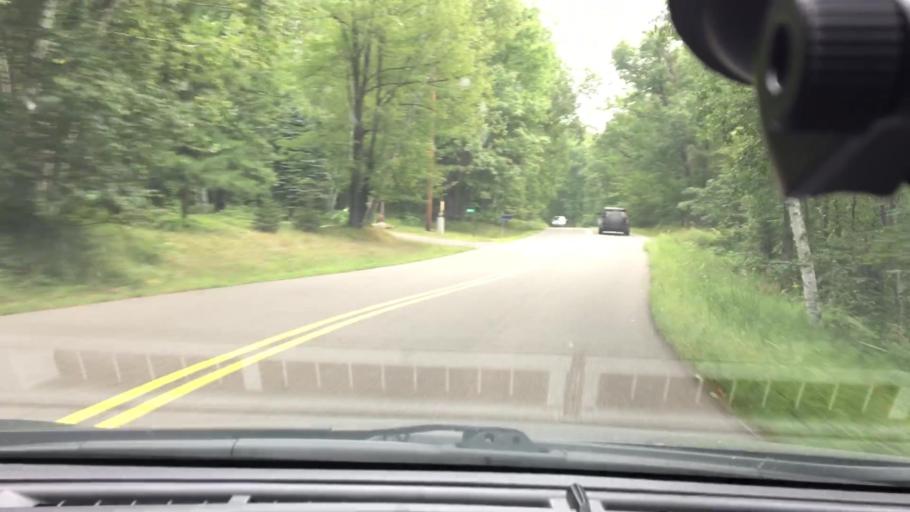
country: US
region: Minnesota
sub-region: Crow Wing County
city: Cross Lake
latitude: 46.6726
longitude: -94.0389
